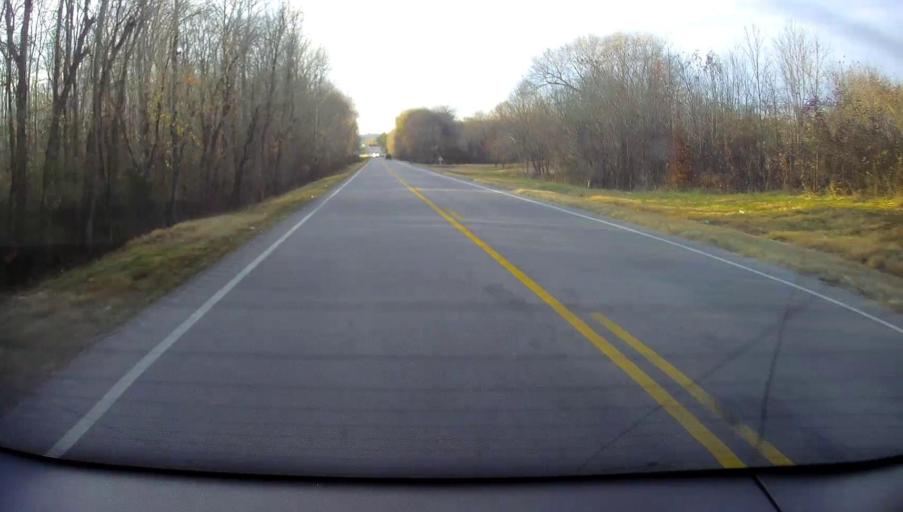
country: US
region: Alabama
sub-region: Blount County
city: Blountsville
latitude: 34.1559
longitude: -86.4609
